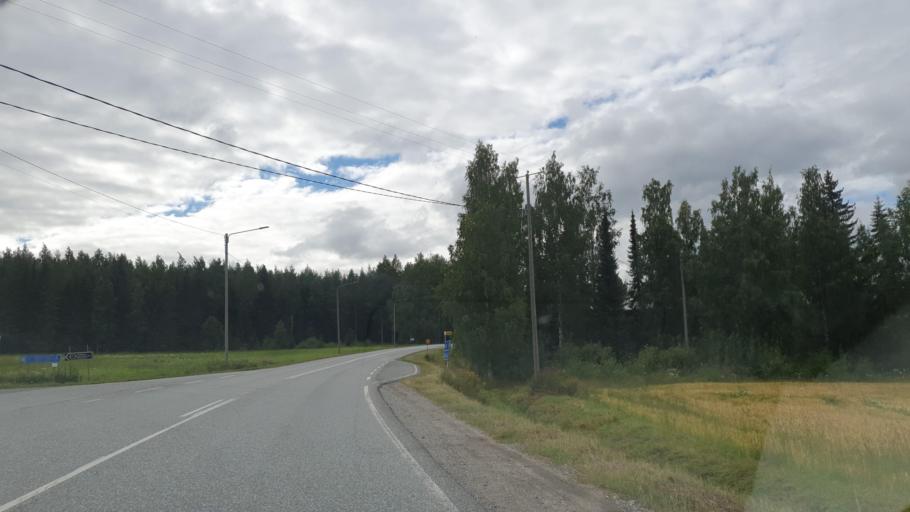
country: FI
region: Northern Savo
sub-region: Ylae-Savo
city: Iisalmi
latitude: 63.5193
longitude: 27.2055
